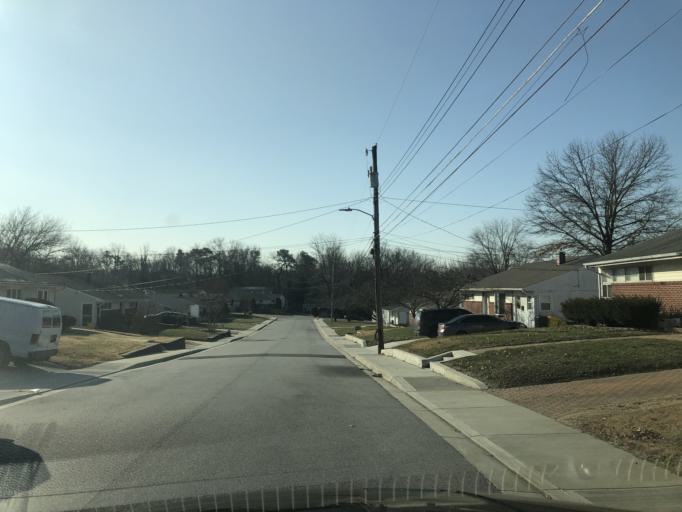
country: US
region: Maryland
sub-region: Anne Arundel County
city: Odenton
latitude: 39.0754
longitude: -76.6978
